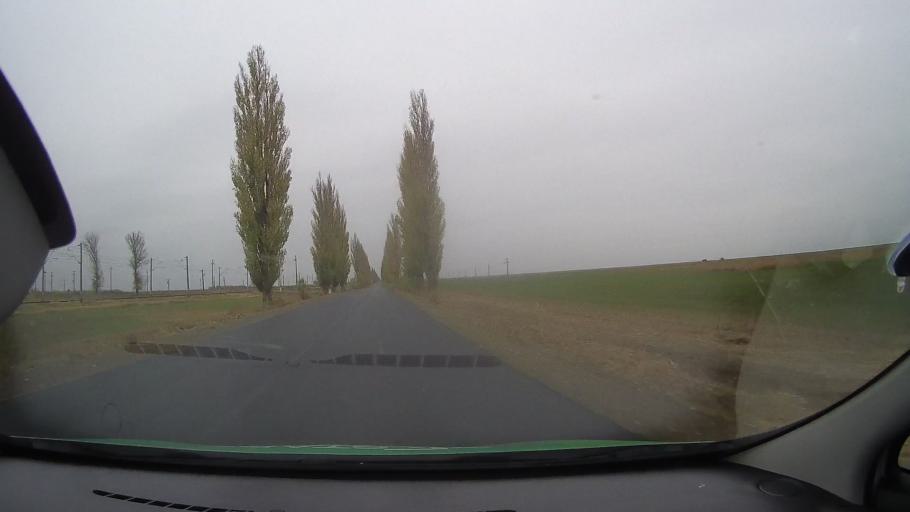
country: RO
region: Ialomita
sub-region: Comuna Valea Ciorii
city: Valea Ciorii
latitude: 44.7120
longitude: 27.5916
